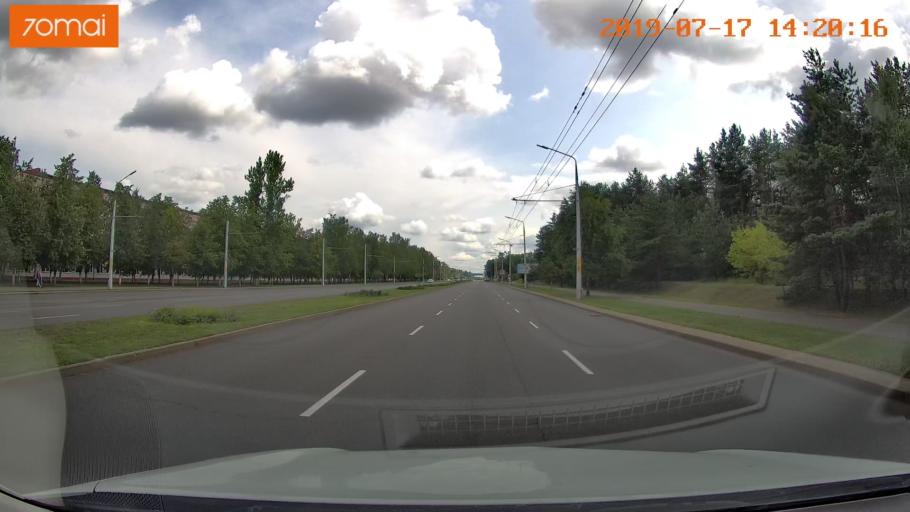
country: BY
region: Mogilev
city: Babruysk
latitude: 53.1820
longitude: 29.1942
